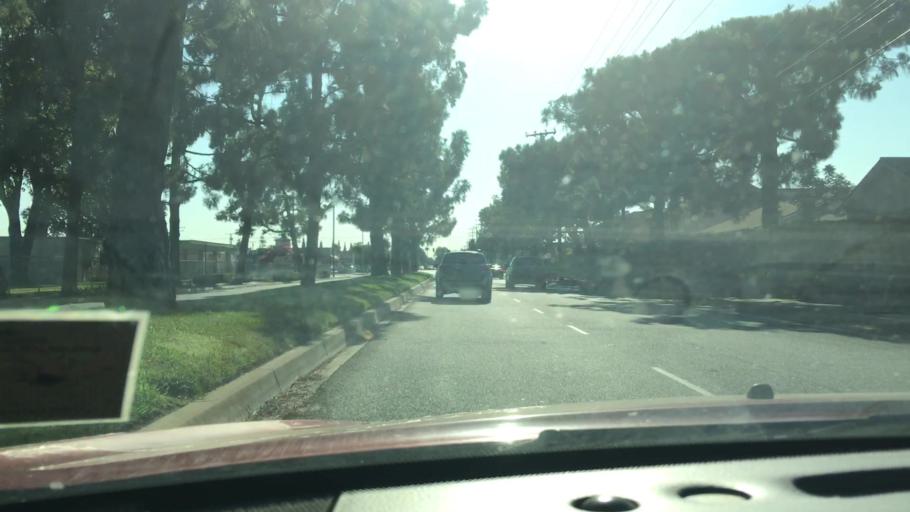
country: US
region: California
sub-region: Los Angeles County
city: Cerritos
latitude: 33.8732
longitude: -118.0690
